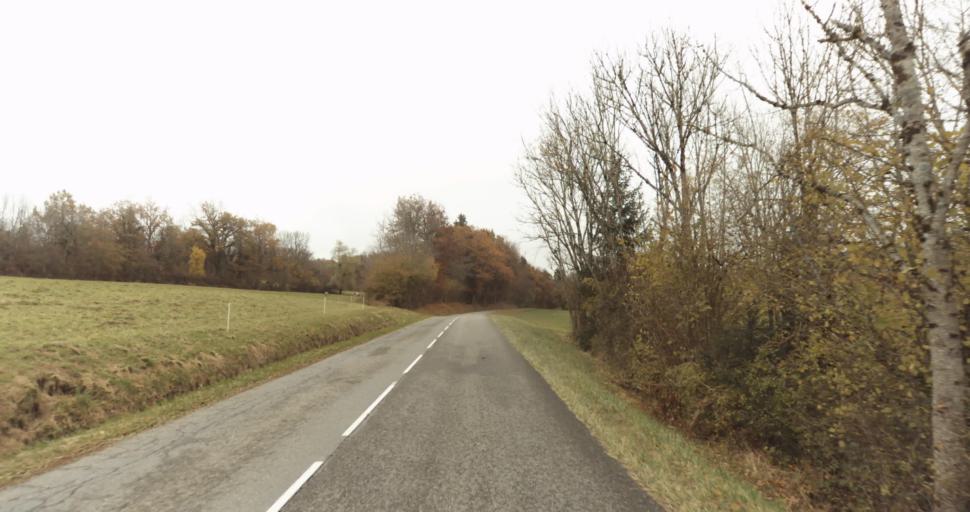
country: FR
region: Rhone-Alpes
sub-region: Departement de la Haute-Savoie
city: Evires
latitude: 46.0259
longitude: 6.2030
